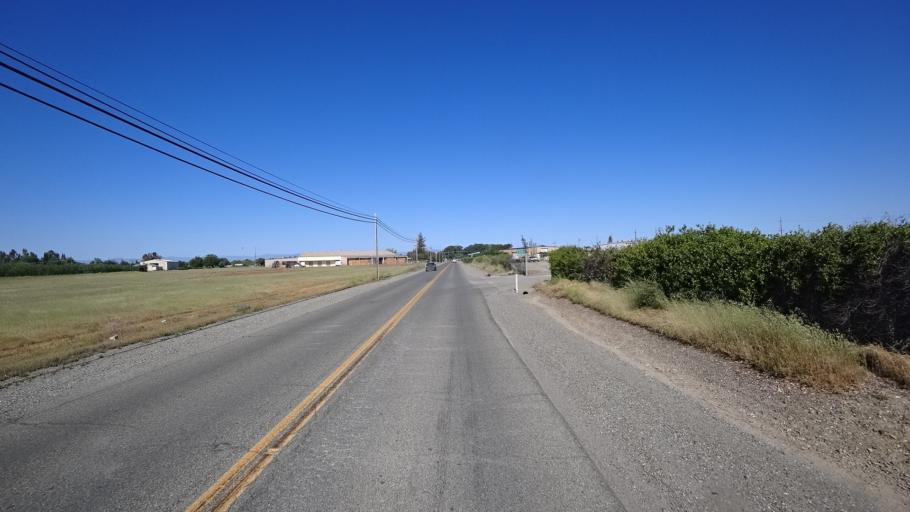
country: US
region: California
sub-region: Glenn County
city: Orland
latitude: 39.7383
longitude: -122.1738
